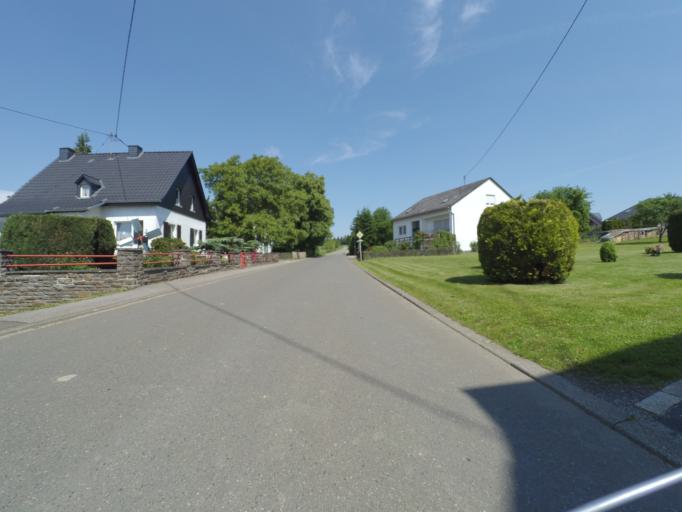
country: DE
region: Rheinland-Pfalz
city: Spesenroth
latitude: 50.0509
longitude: 7.4595
